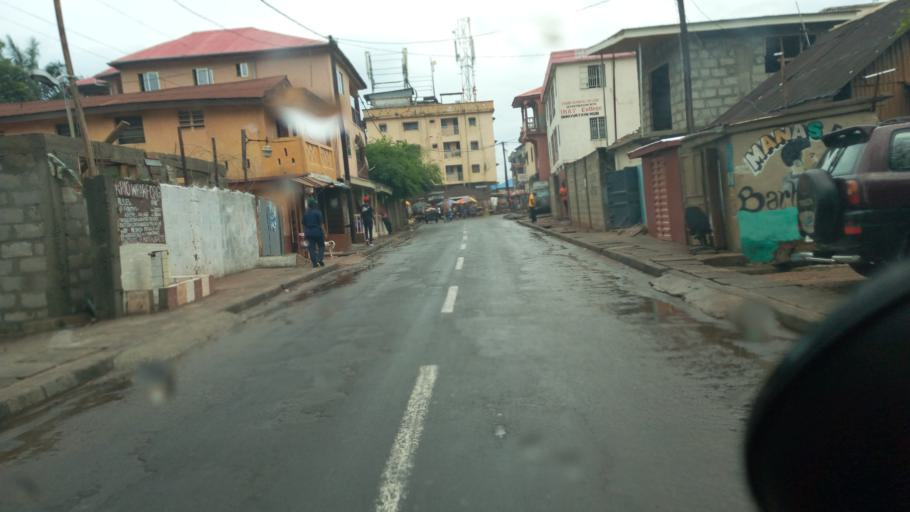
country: SL
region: Western Area
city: Freetown
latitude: 8.4753
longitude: -13.2395
